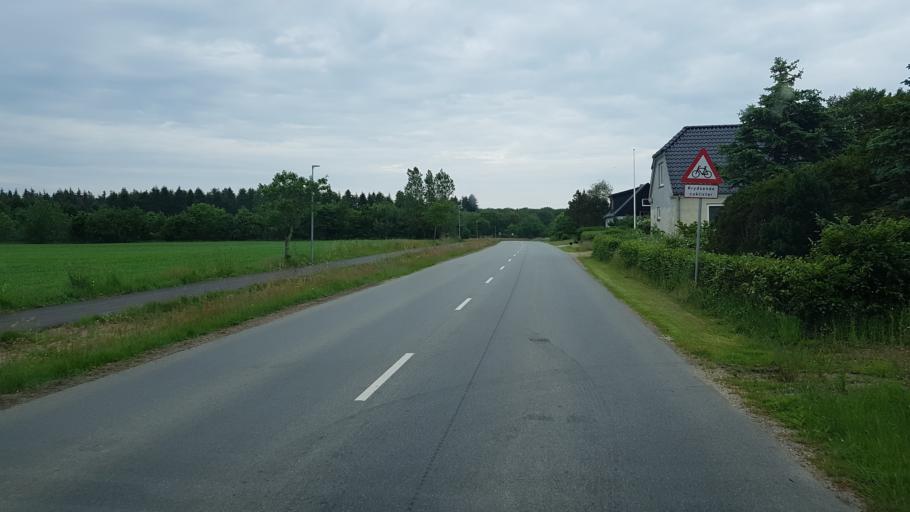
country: DK
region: South Denmark
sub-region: Varde Kommune
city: Oksbol
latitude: 55.6460
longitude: 8.2851
